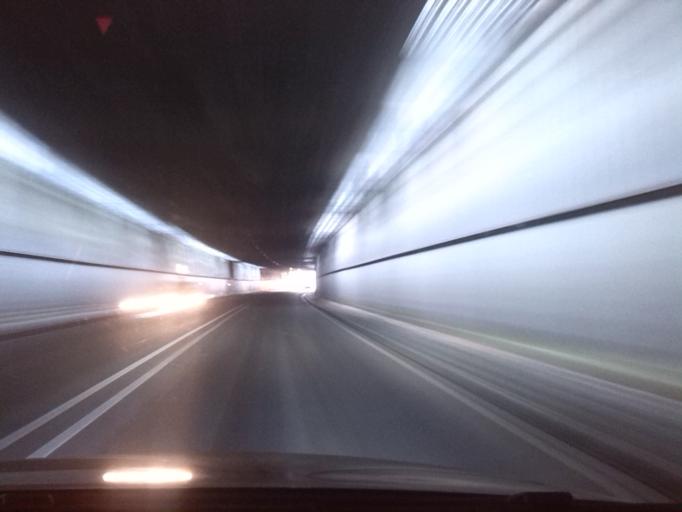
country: DE
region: Baden-Wuerttemberg
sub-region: Regierungsbezirk Stuttgart
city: Stuttgart Muehlhausen
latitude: 48.8296
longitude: 9.2359
